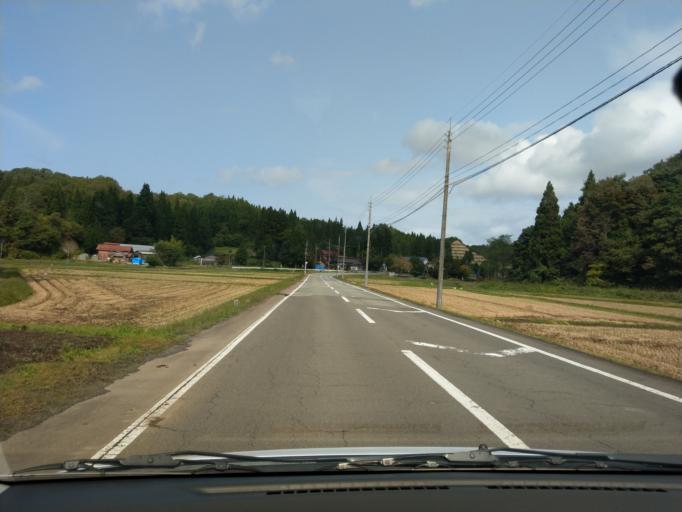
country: JP
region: Akita
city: Omagari
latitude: 39.5039
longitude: 140.3124
